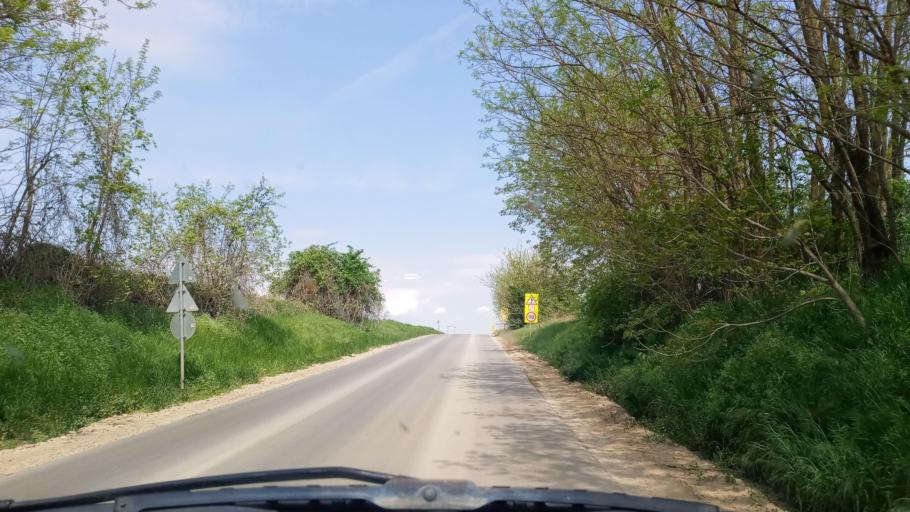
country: HU
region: Baranya
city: Boly
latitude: 45.9252
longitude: 18.5456
